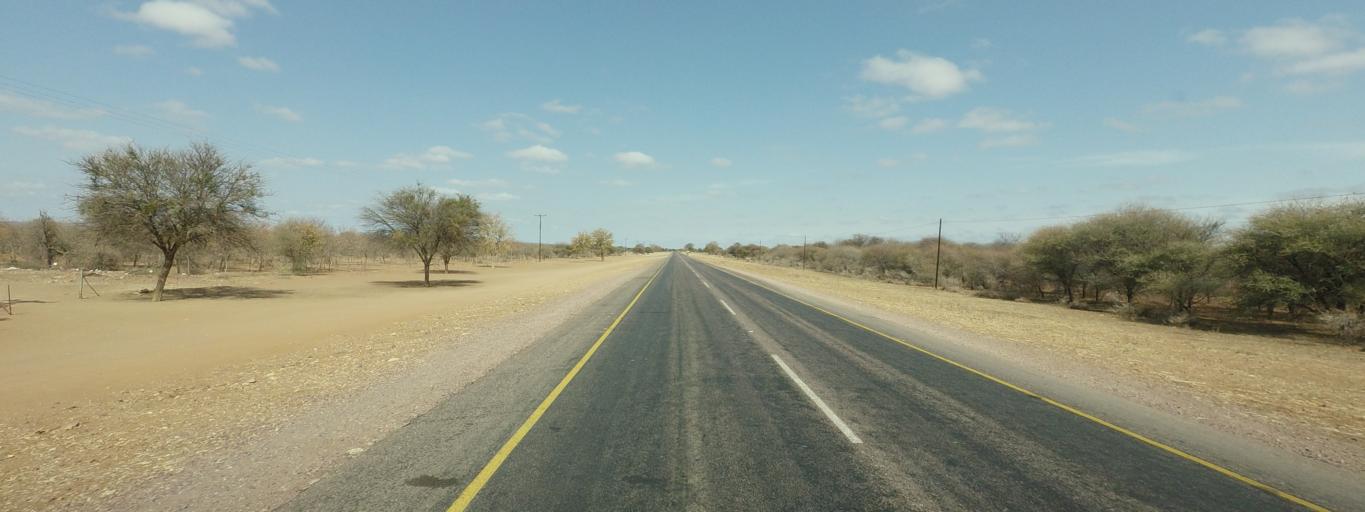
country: BW
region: Central
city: Ramokgonami
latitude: -22.7883
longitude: 27.4368
